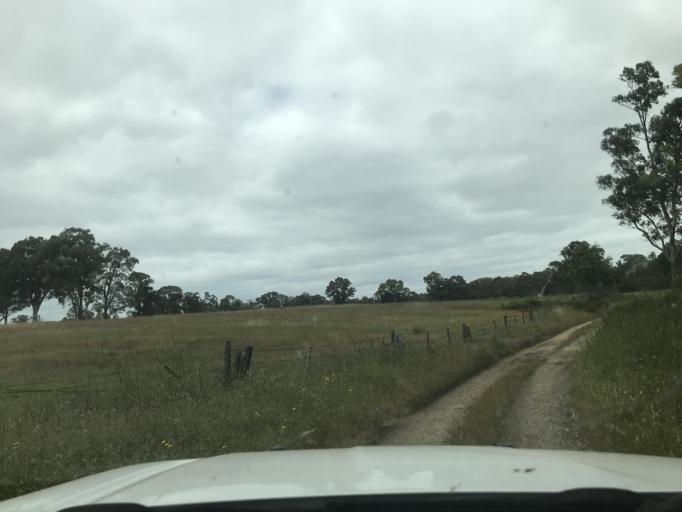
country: AU
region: South Australia
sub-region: Wattle Range
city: Penola
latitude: -37.1932
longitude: 140.9731
